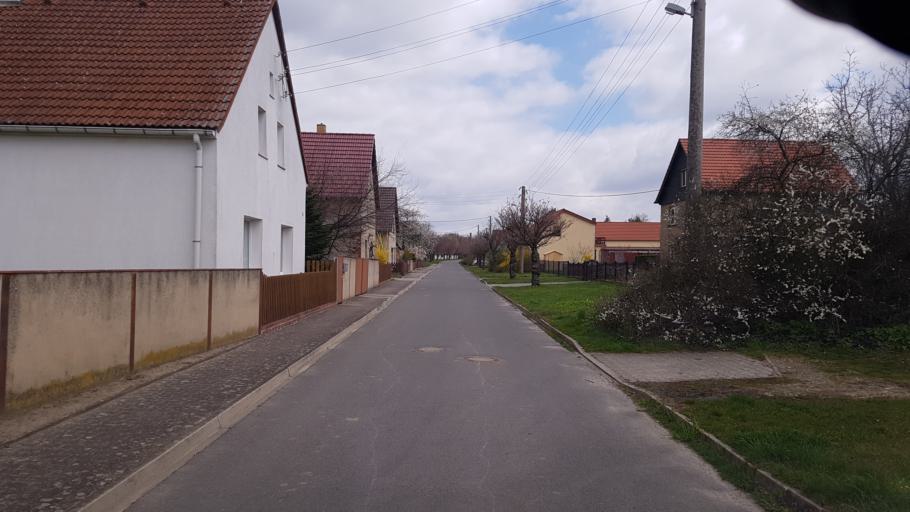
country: DE
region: Brandenburg
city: Plessa
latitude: 51.4849
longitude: 13.5892
